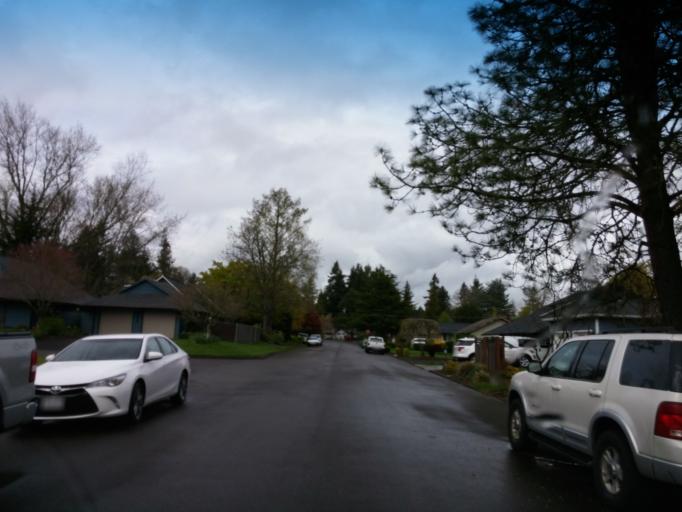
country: US
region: Oregon
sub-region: Washington County
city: Cedar Mill
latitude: 45.5159
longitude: -122.8258
